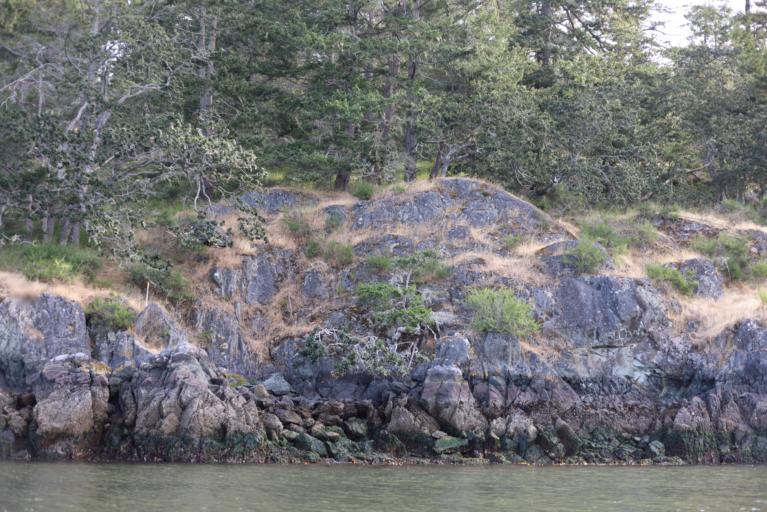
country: CA
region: British Columbia
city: Metchosin
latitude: 48.3448
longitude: -123.5616
